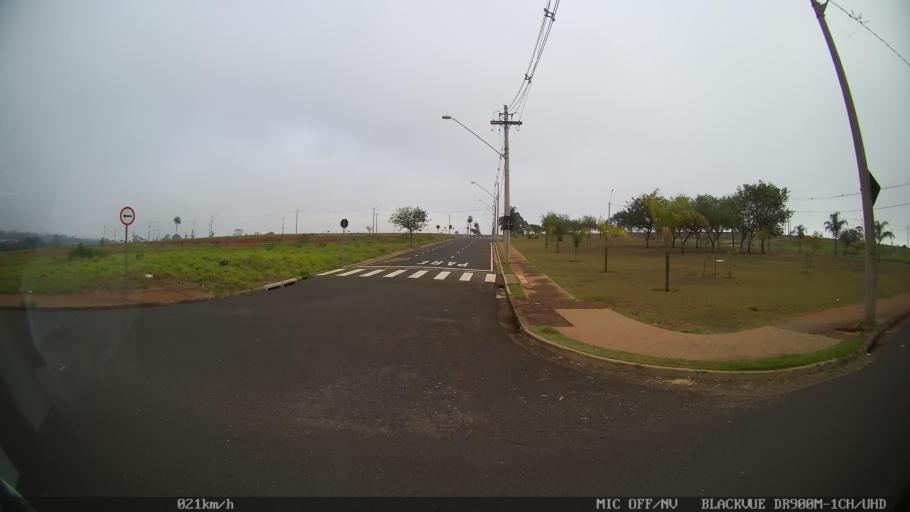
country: BR
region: Sao Paulo
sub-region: Sao Jose Do Rio Preto
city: Sao Jose do Rio Preto
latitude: -20.8557
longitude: -49.3720
